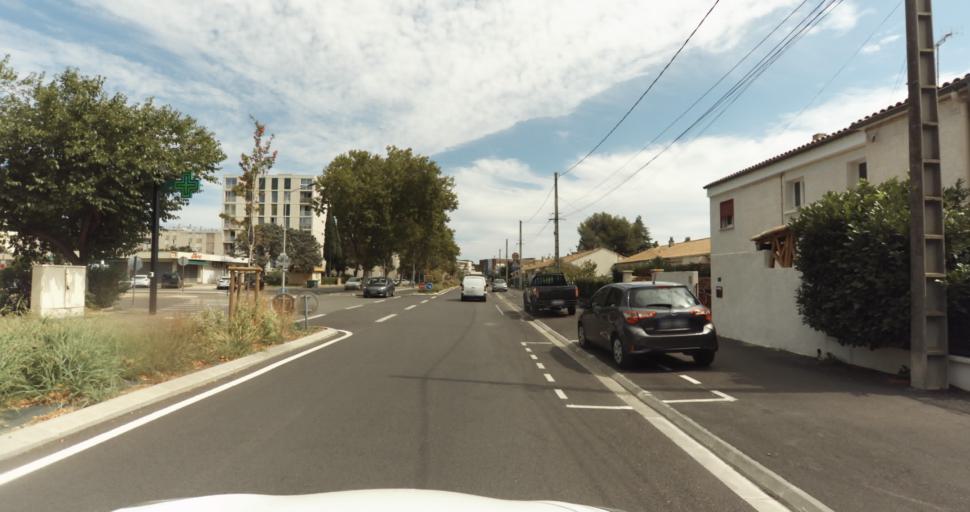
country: FR
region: Provence-Alpes-Cote d'Azur
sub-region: Departement des Bouches-du-Rhone
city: Miramas
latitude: 43.5874
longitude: 5.0044
